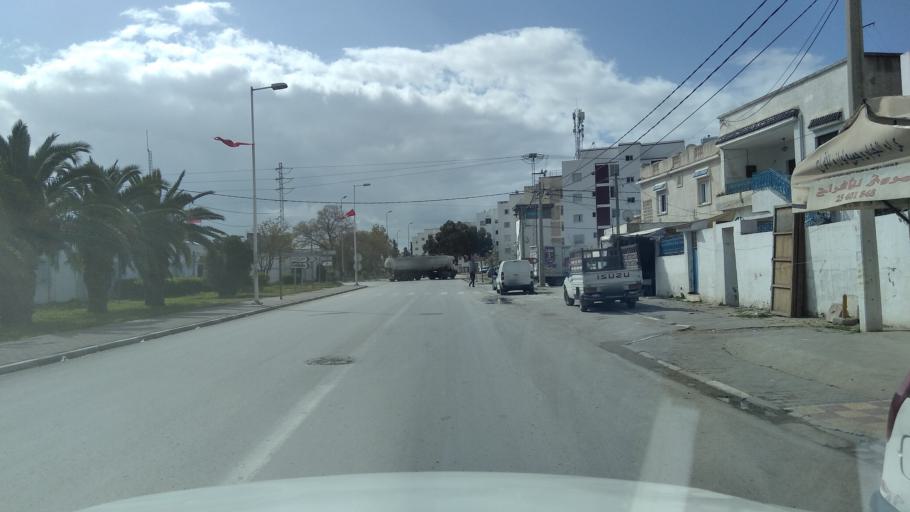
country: TN
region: Bin 'Arus
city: Ben Arous
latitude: 36.7449
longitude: 10.2260
